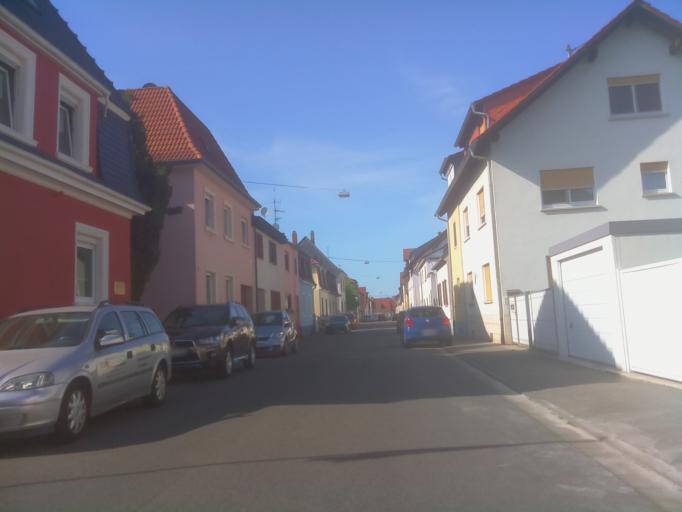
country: DE
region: Baden-Wuerttemberg
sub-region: Karlsruhe Region
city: Edingen-Neckarhausen
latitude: 49.4647
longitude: 8.5979
